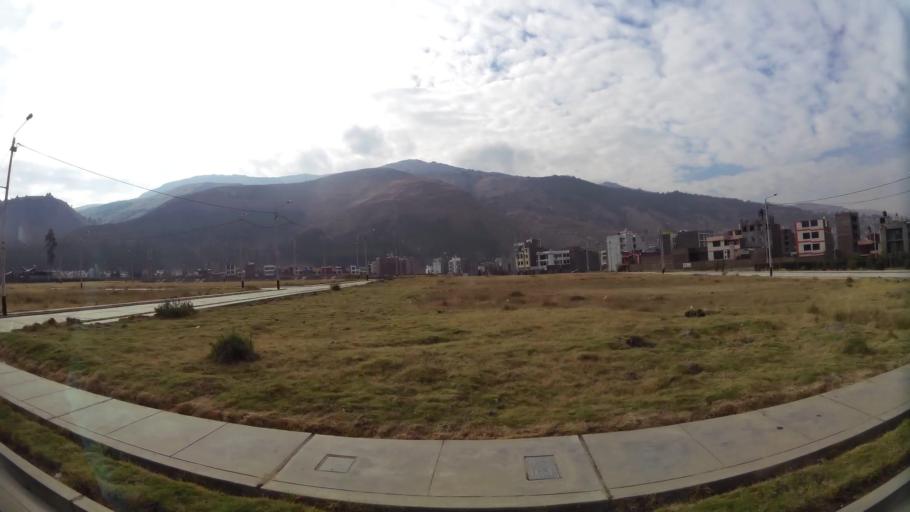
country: PE
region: Junin
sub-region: Provincia de Huancayo
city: Huancayo
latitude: -12.0474
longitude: -75.1920
